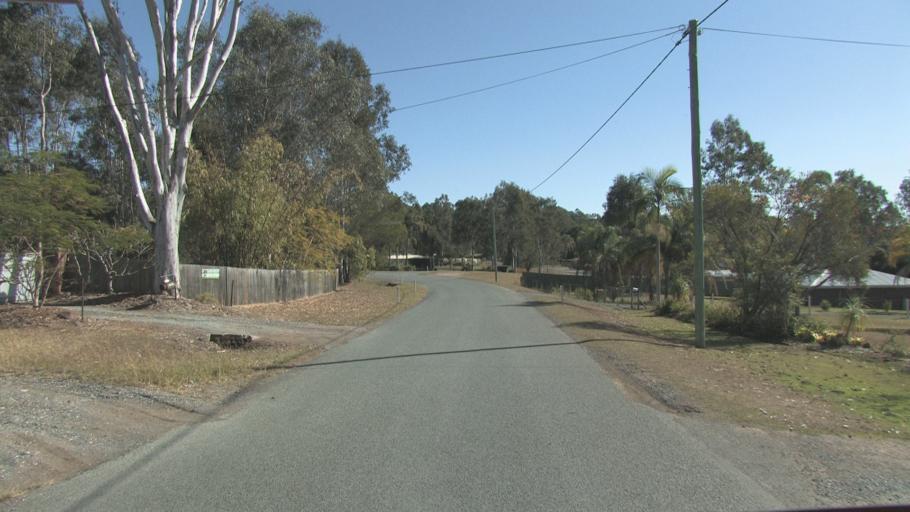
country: AU
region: Queensland
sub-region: Logan
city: Cedar Vale
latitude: -27.8523
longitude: 153.0181
